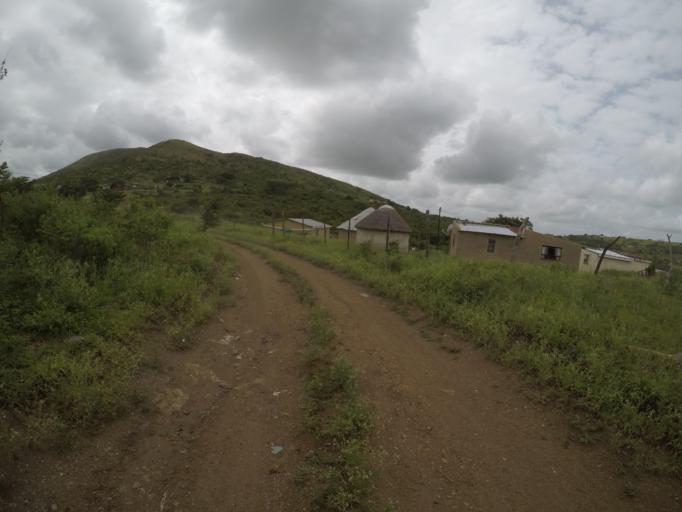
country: ZA
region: KwaZulu-Natal
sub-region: uThungulu District Municipality
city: Empangeni
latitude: -28.6083
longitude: 31.8927
